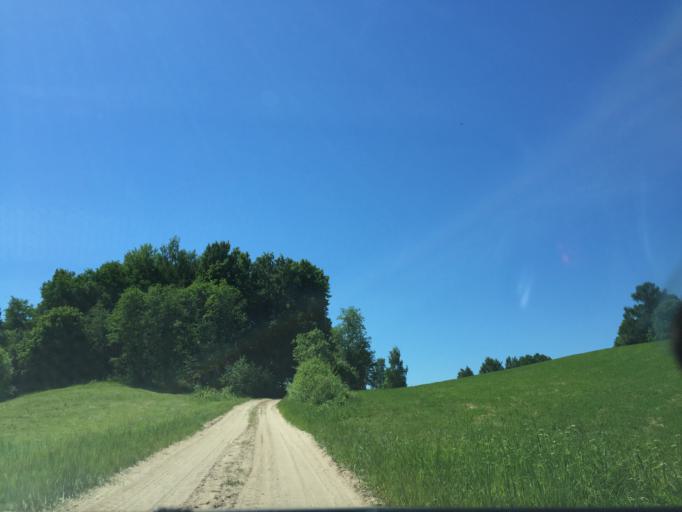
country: LV
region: Preilu Rajons
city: Jaunaglona
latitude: 56.2308
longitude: 27.2290
